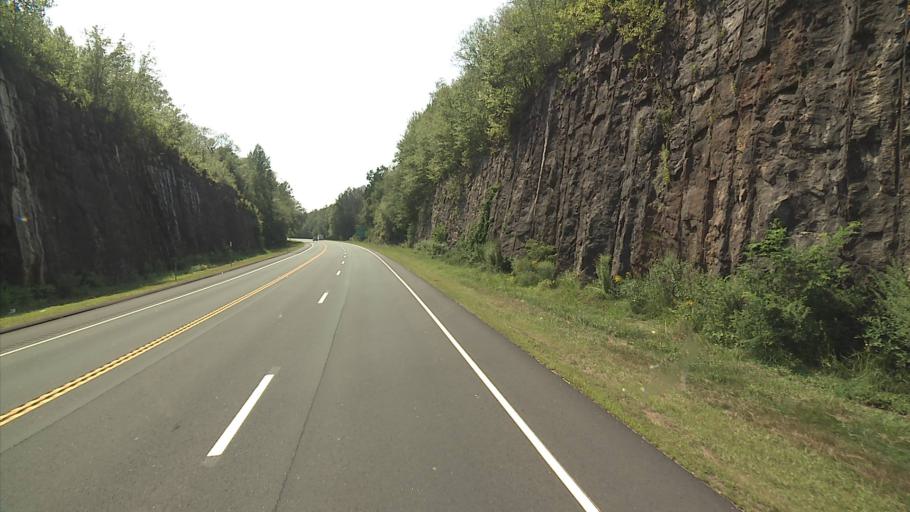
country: US
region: Connecticut
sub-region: Middlesex County
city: East Haddam
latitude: 41.4394
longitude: -72.4840
